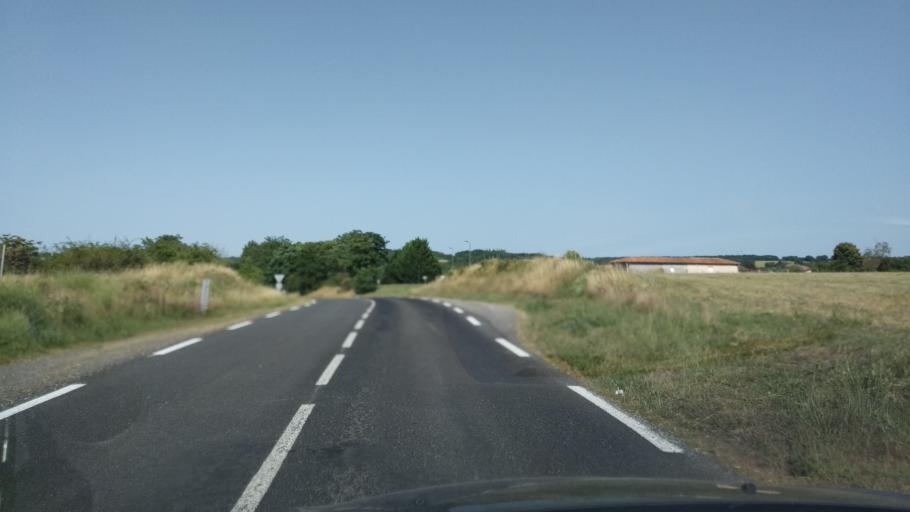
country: FR
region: Poitou-Charentes
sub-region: Departement de la Vienne
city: Lussac-les-Chateaux
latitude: 46.4443
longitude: 0.6567
